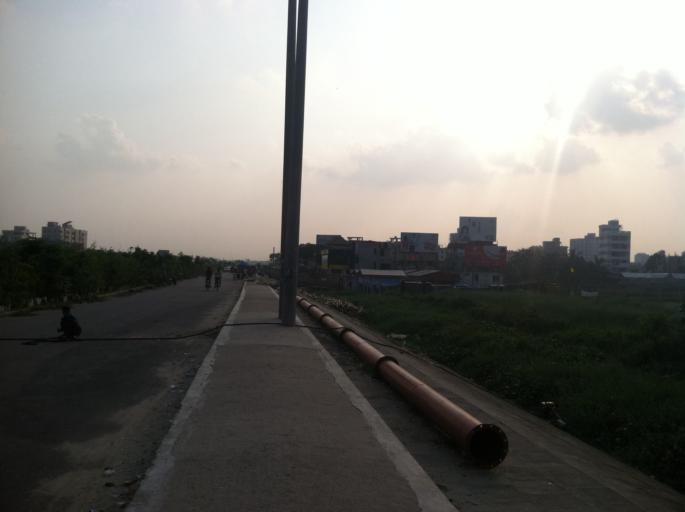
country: BD
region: Dhaka
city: Tungi
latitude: 23.8280
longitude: 90.4344
